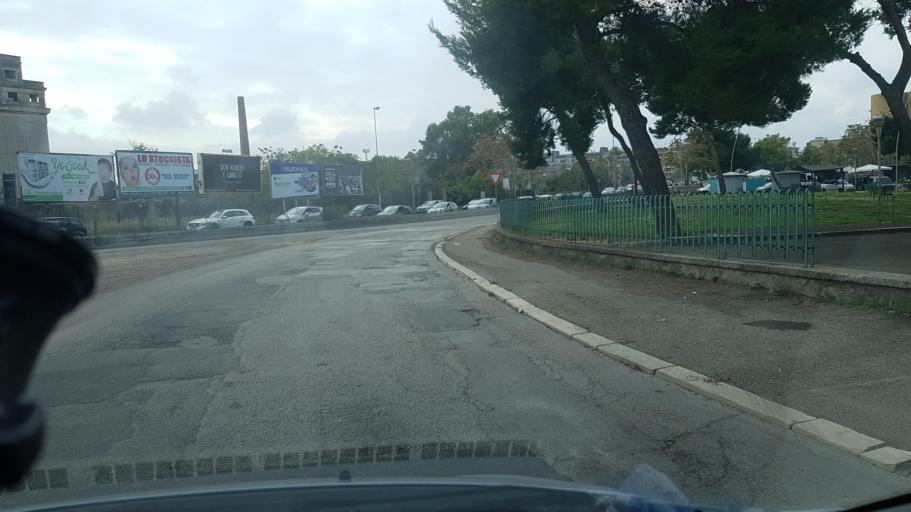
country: IT
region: Apulia
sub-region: Provincia di Foggia
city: Foggia
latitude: 41.4712
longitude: 15.5498
